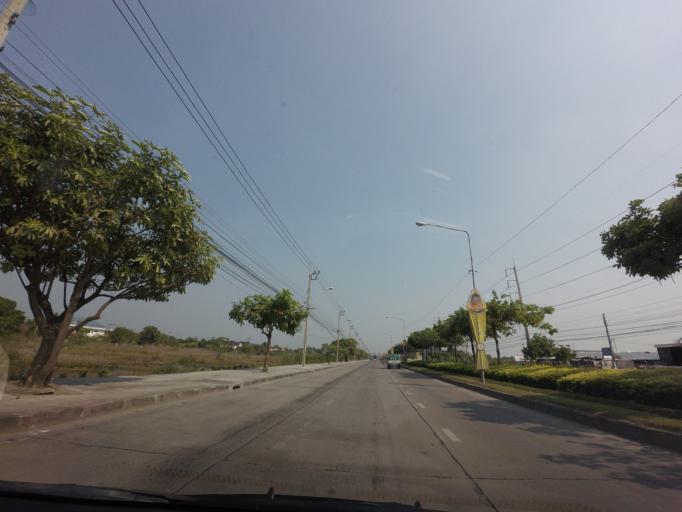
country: TH
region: Bangkok
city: Lat Krabang
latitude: 13.7519
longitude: 100.7833
